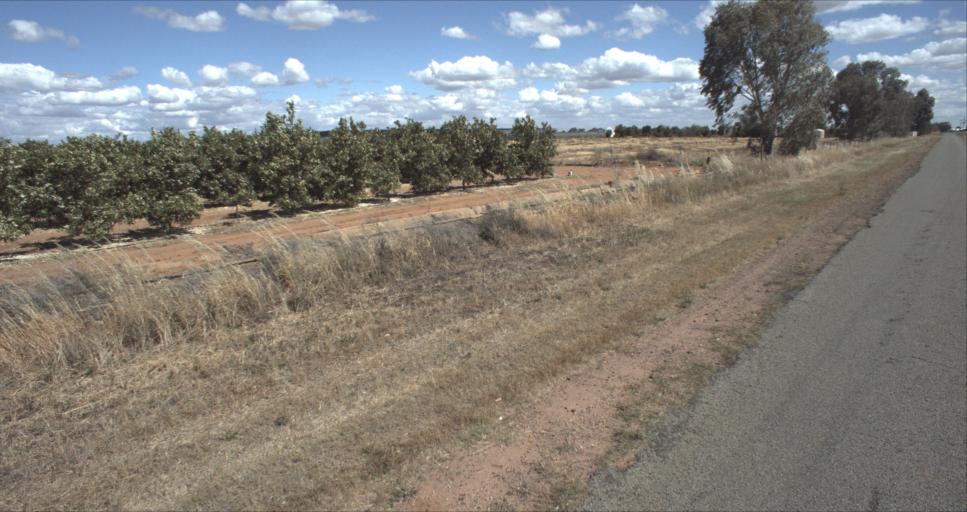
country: AU
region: New South Wales
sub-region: Leeton
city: Leeton
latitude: -34.5148
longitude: 146.2390
